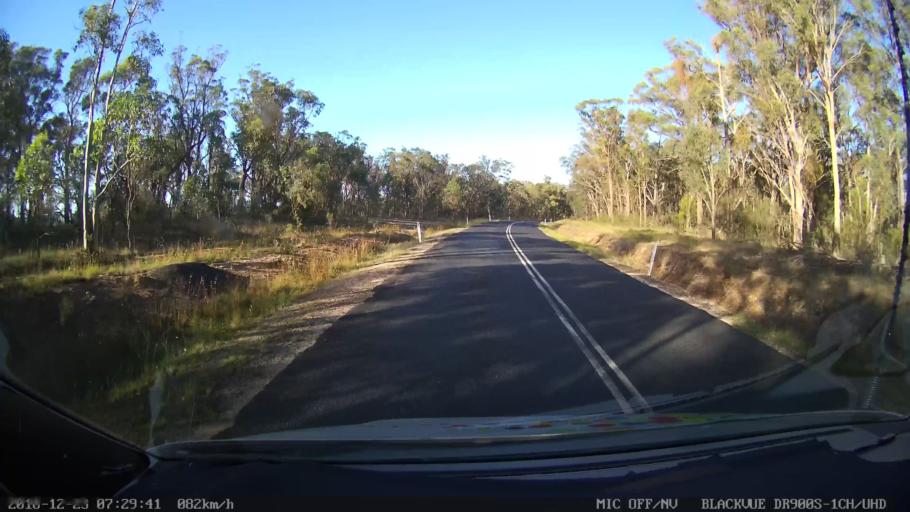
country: AU
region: New South Wales
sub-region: Armidale Dumaresq
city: Enmore
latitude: -30.4974
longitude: 152.1535
